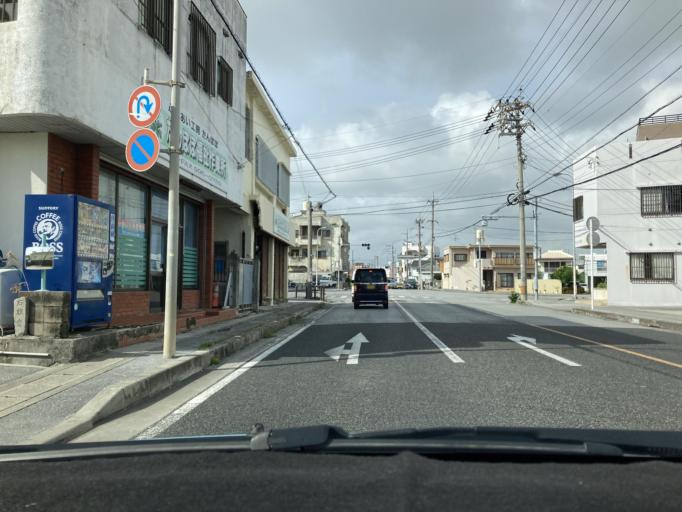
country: JP
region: Okinawa
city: Itoman
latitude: 26.1252
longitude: 127.6696
